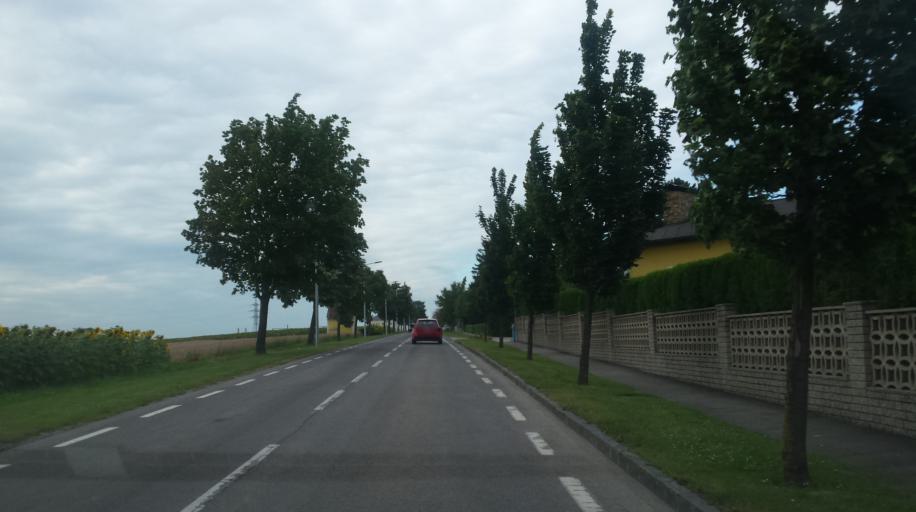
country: AT
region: Lower Austria
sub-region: Politischer Bezirk Wien-Umgebung
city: Moosbrunn
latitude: 48.0227
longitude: 16.4622
